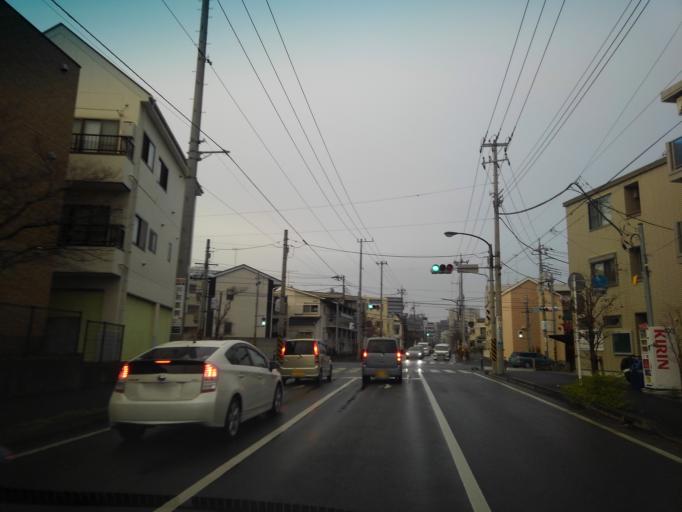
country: JP
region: Tokyo
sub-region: Machida-shi
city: Machida
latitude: 35.5252
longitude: 139.4392
